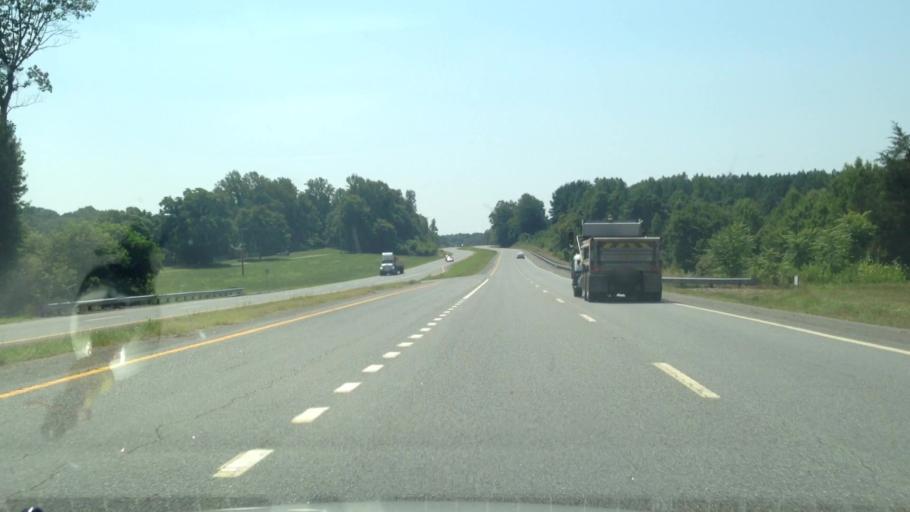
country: US
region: Virginia
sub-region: Patrick County
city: Patrick Springs
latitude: 36.5954
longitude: -80.1536
